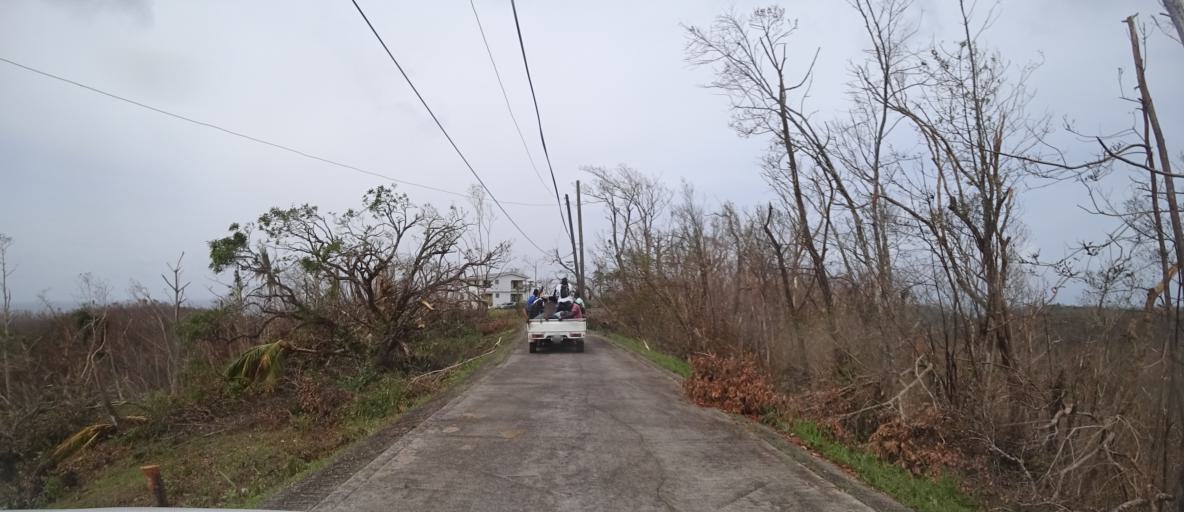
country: DM
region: Saint Andrew
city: Calibishie
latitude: 15.5889
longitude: -61.3709
